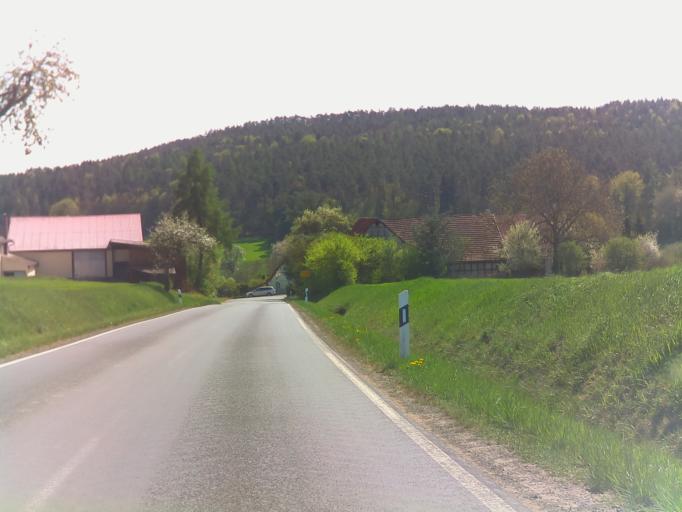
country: DE
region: Bavaria
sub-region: Regierungsbezirk Unterfranken
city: Burgpreppach
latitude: 50.1547
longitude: 10.6354
